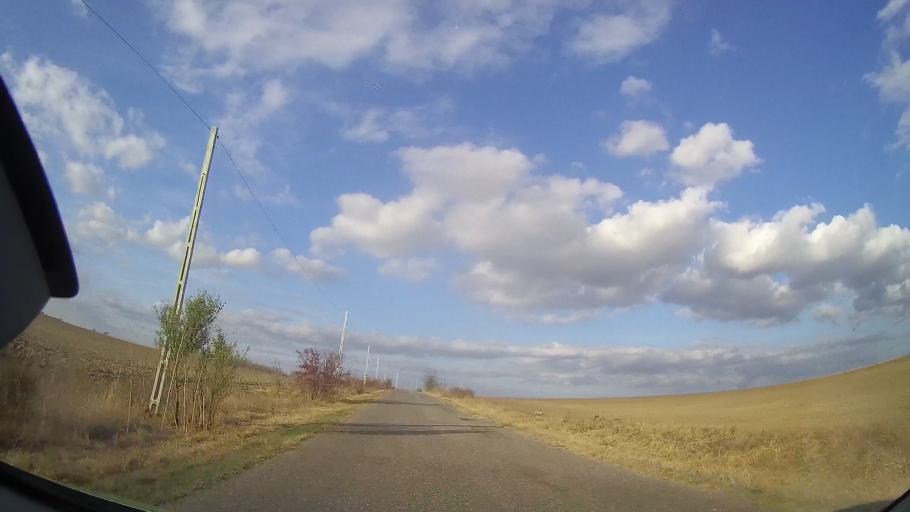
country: RO
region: Constanta
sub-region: Comuna Cerchezu
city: Cerchezu
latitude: 43.8444
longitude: 28.0984
